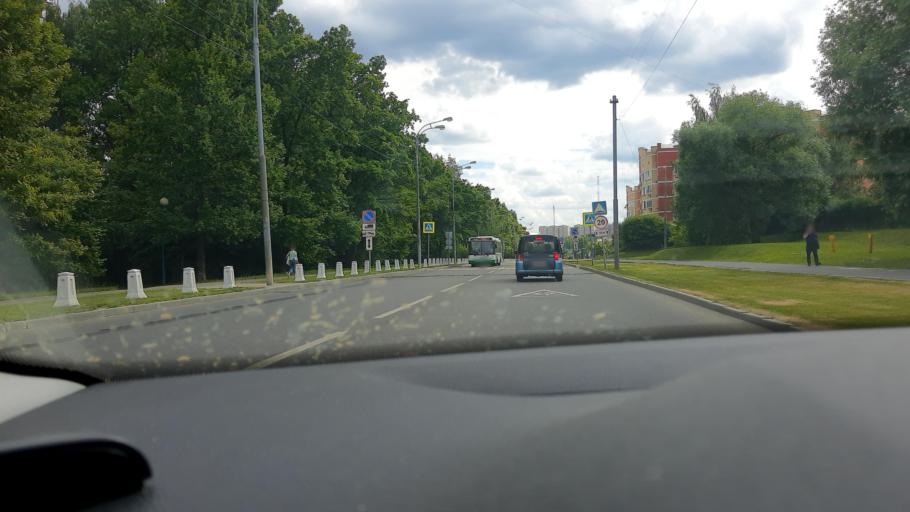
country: RU
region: Moscow
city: Khimki
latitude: 55.8915
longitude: 37.3994
